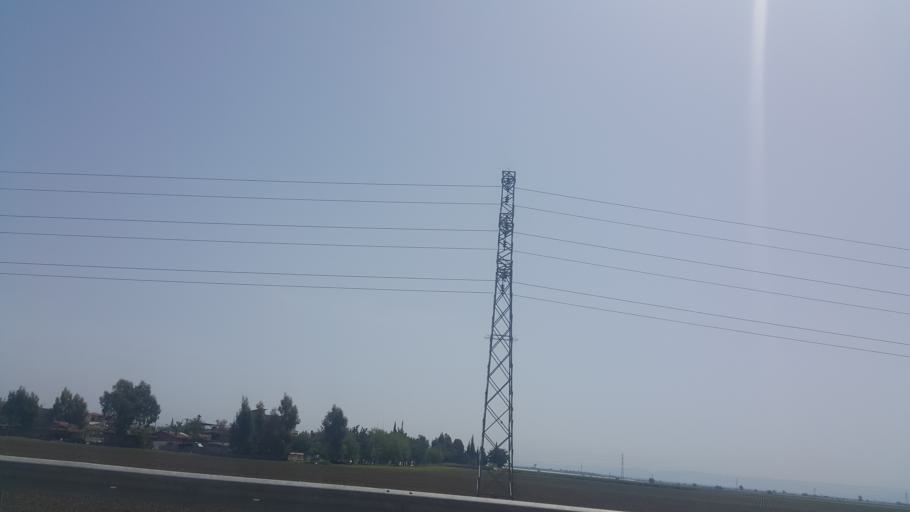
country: TR
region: Hatay
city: Serinyol
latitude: 36.3843
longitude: 36.2303
